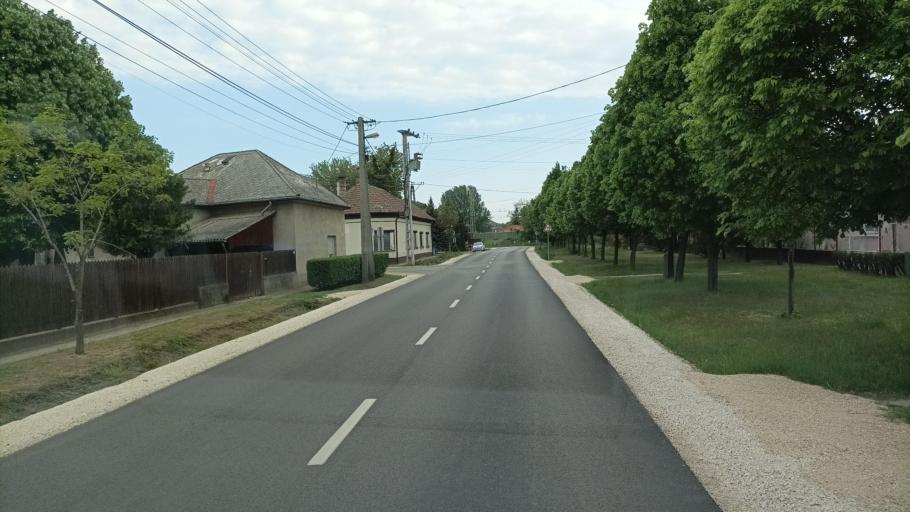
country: HU
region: Pest
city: Pilis
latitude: 47.2808
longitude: 19.5333
